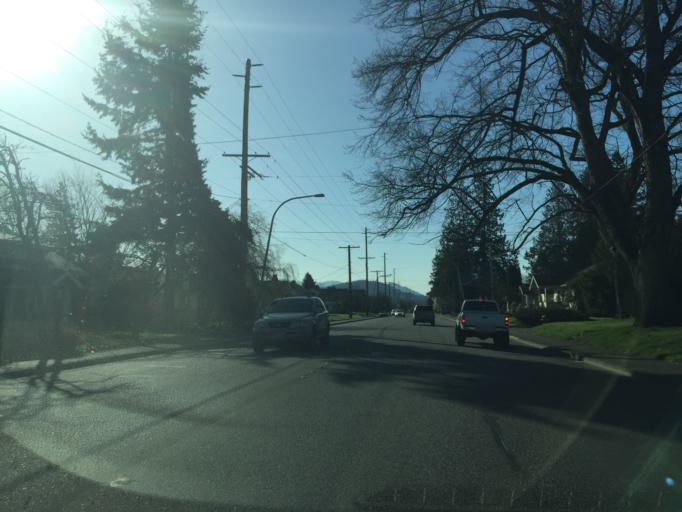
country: US
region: Washington
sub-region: Whatcom County
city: Bellingham
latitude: 48.7714
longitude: -122.4861
